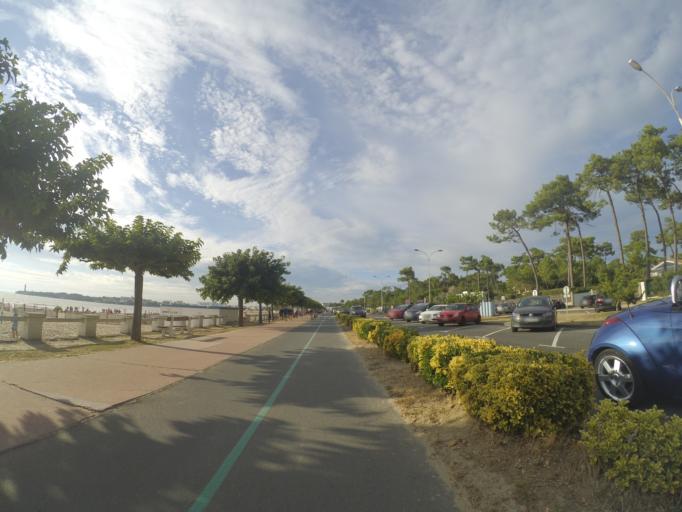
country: FR
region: Poitou-Charentes
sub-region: Departement de la Charente-Maritime
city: Saint-Georges-de-Didonne
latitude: 45.5939
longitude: -0.9913
